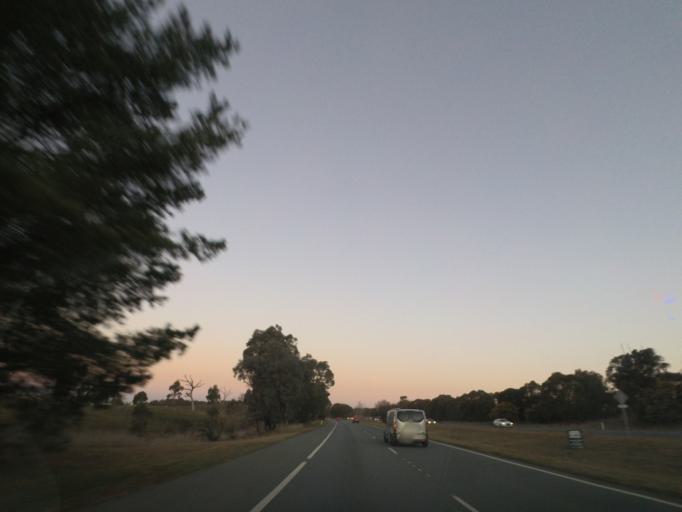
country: AU
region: Australian Capital Territory
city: Kaleen
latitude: -35.2044
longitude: 149.0991
